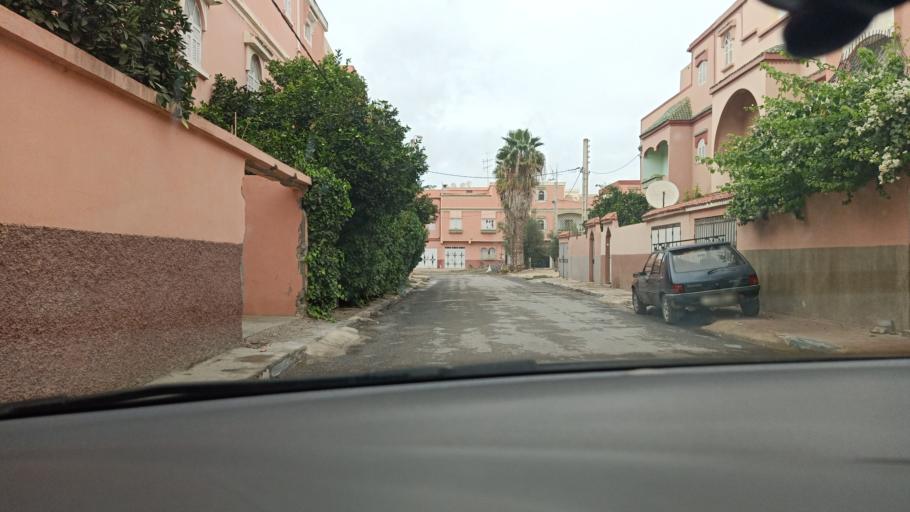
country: MA
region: Doukkala-Abda
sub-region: Safi
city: Youssoufia
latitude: 32.2534
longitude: -8.5369
